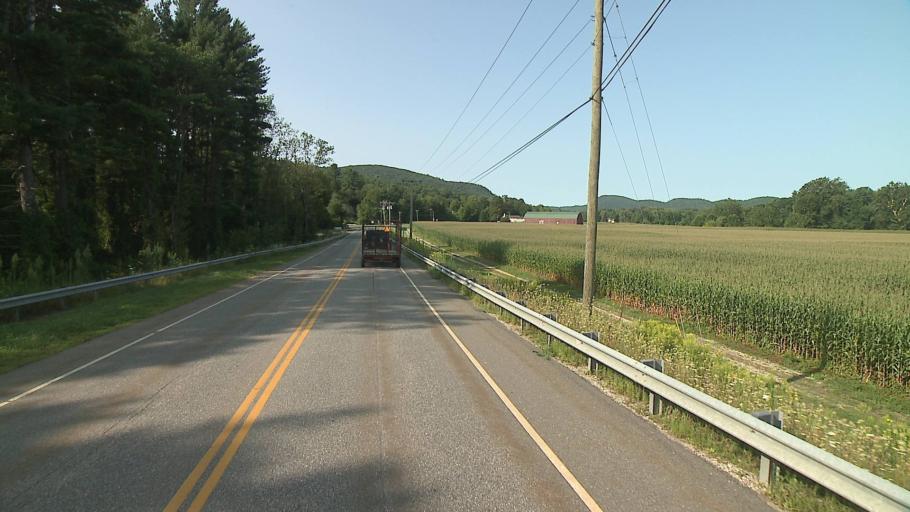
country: US
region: Connecticut
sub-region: Litchfield County
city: Canaan
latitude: 41.9338
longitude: -73.3625
